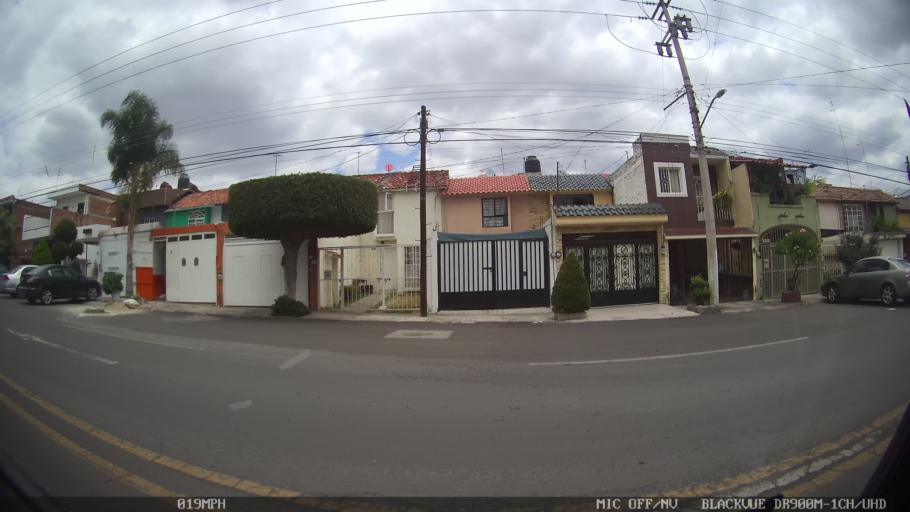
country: MX
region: Jalisco
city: Tonala
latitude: 20.6341
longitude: -103.2608
